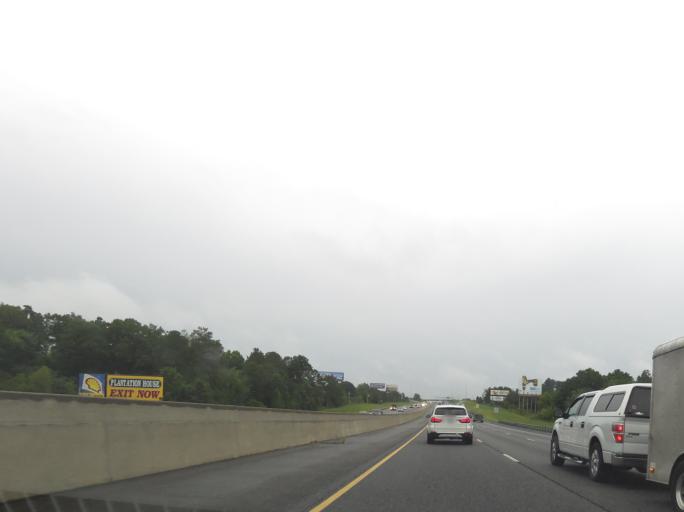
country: US
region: Georgia
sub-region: Crisp County
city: Cordele
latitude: 31.8450
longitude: -83.7164
